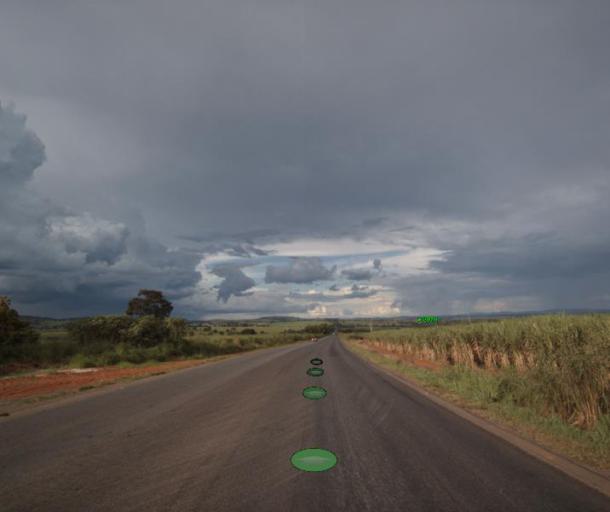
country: BR
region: Goias
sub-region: Ceres
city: Ceres
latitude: -15.1435
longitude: -49.5295
